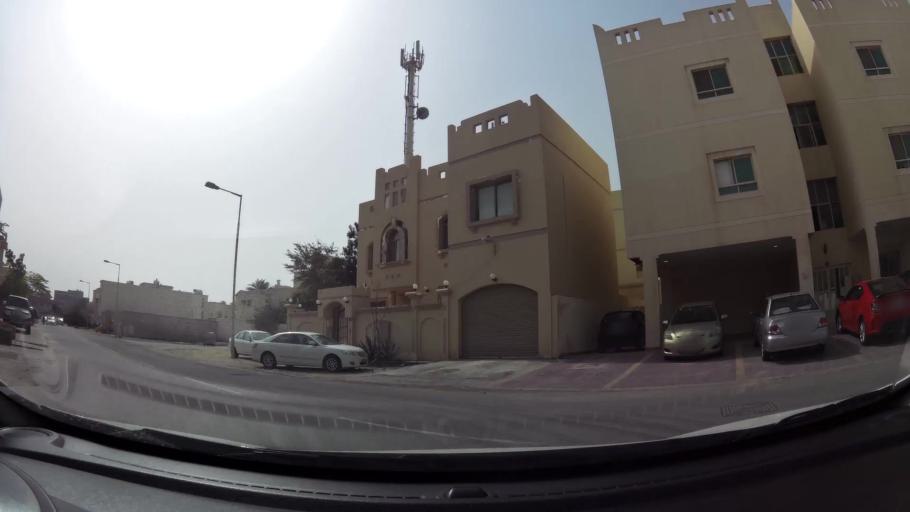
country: BH
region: Manama
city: Jidd Hafs
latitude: 26.2331
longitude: 50.5258
